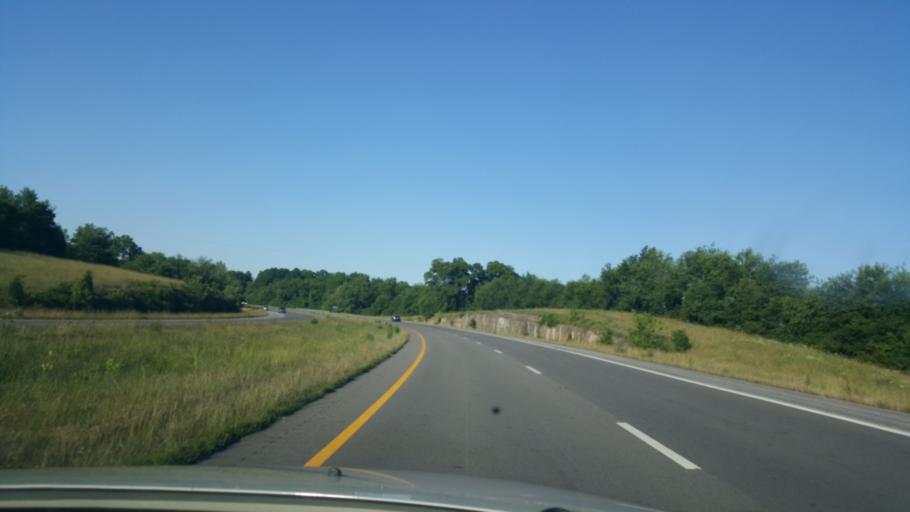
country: US
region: Tennessee
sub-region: Maury County
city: Columbia
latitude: 35.6220
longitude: -87.1173
